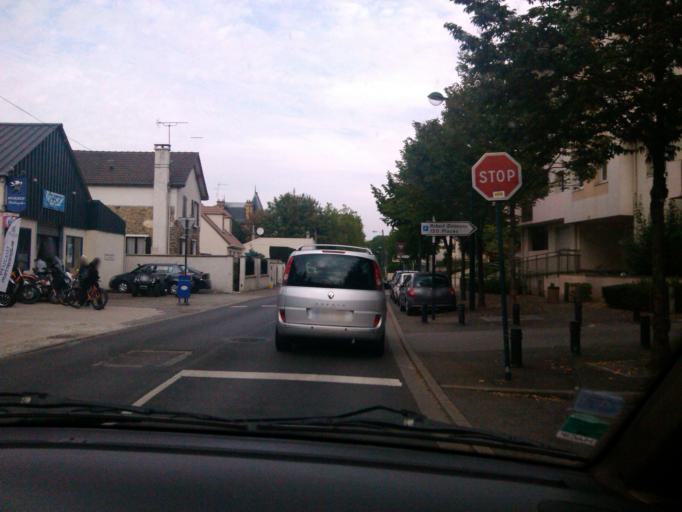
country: FR
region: Ile-de-France
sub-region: Departement des Yvelines
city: Plaisir
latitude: 48.8325
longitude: 1.9416
